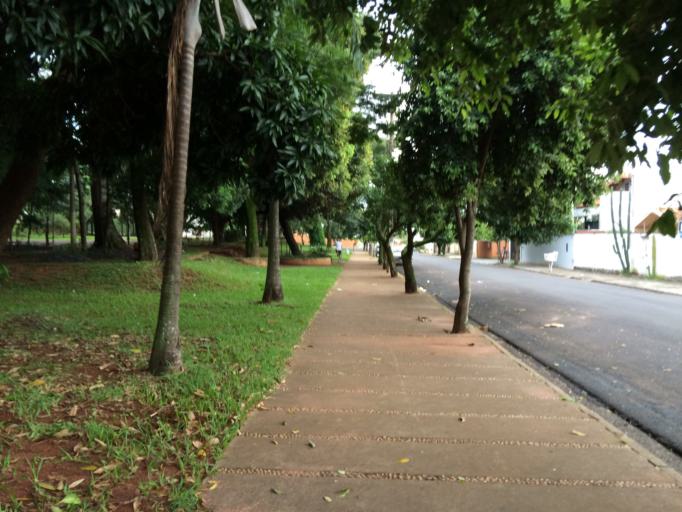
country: BR
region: Sao Paulo
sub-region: Matao
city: Matao
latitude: -21.6111
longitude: -48.3661
